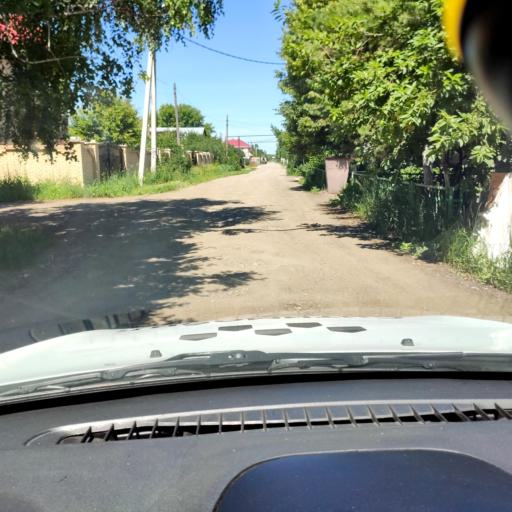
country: RU
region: Samara
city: Tol'yatti
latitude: 53.5661
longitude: 49.3862
